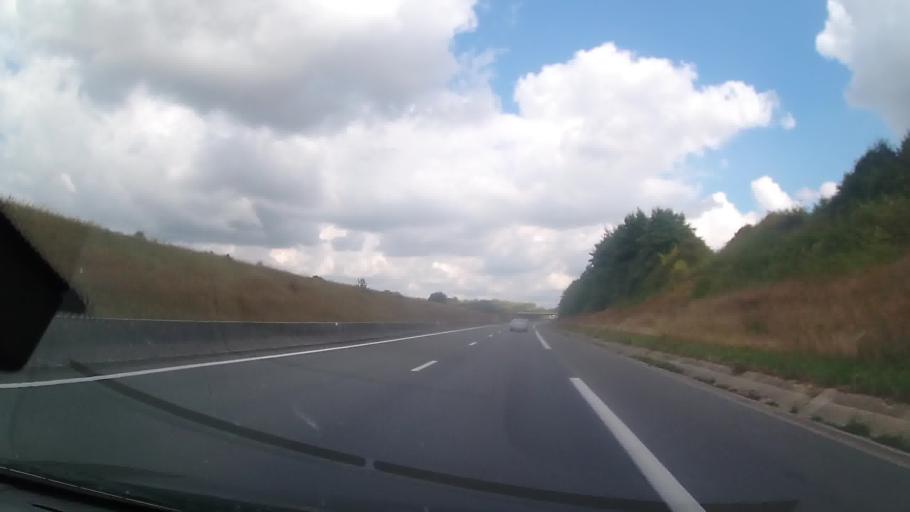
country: FR
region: Nord-Pas-de-Calais
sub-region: Departement du Pas-de-Calais
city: Saint-Josse
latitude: 50.4530
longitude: 1.6959
